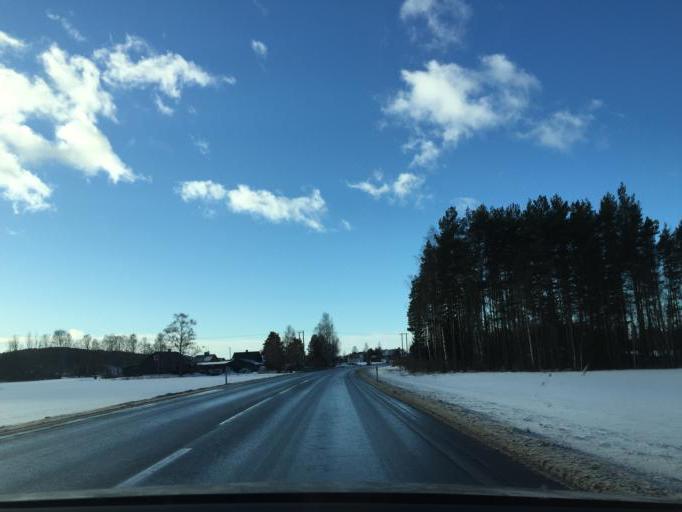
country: NO
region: Hedmark
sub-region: Sor-Odal
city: Skarnes
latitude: 60.2210
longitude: 11.6485
